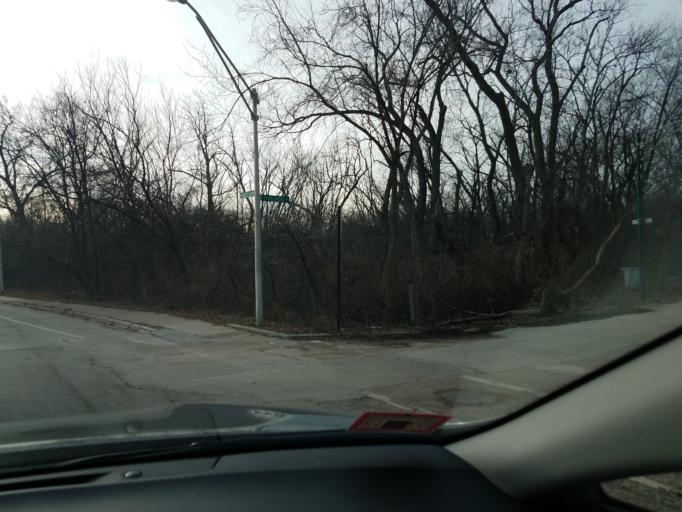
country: US
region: Illinois
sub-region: Cook County
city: Lincolnwood
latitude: 41.9840
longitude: -87.7517
